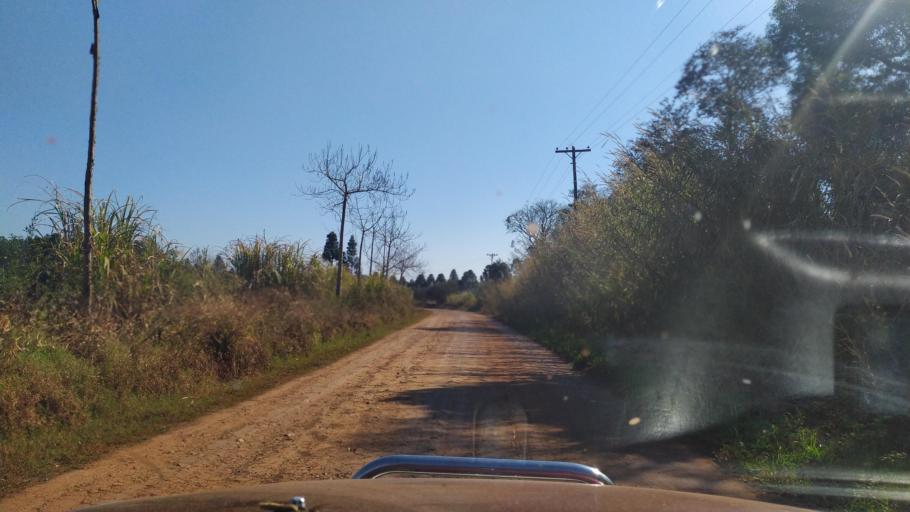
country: AR
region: Misiones
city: El Alcazar
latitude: -26.7151
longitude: -54.6997
